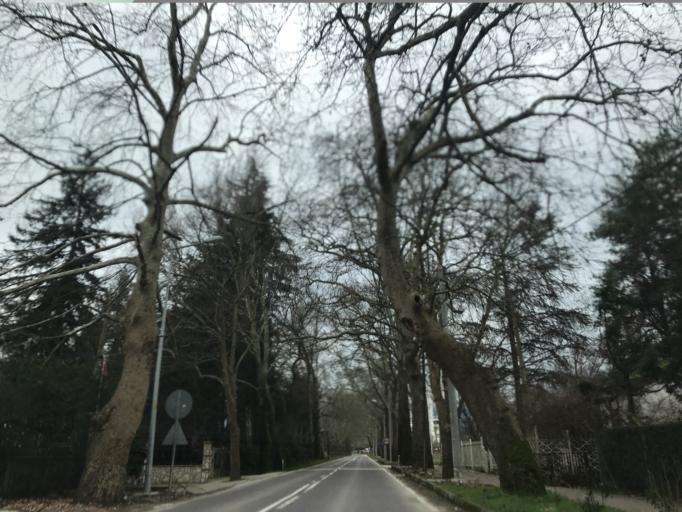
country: TR
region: Yalova
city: Kadikoy
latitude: 40.6342
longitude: 29.2247
